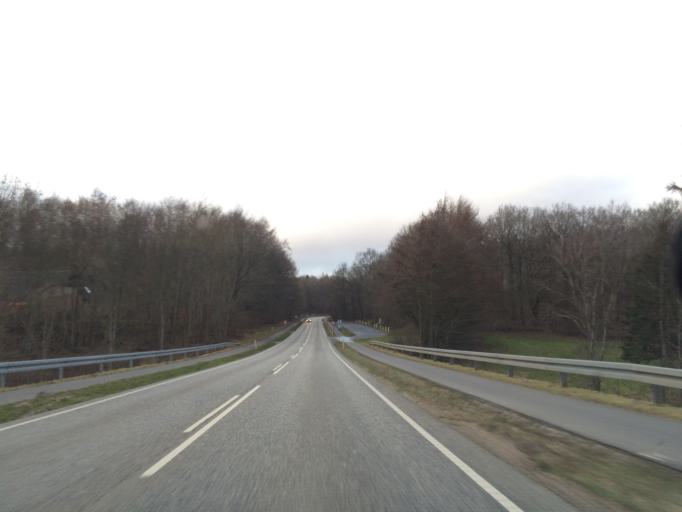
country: DK
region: Central Jutland
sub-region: Silkeborg Kommune
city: Virklund
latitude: 56.1128
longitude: 9.5686
